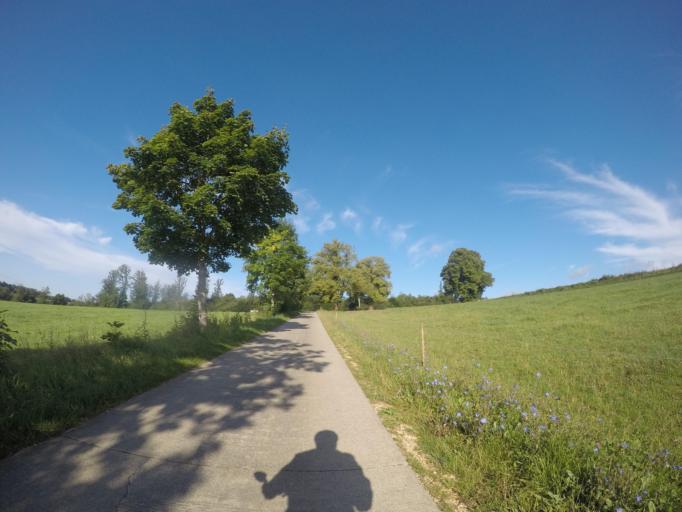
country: DE
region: Baden-Wuerttemberg
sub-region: Tuebingen Region
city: Schelklingen
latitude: 48.3931
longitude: 9.7333
